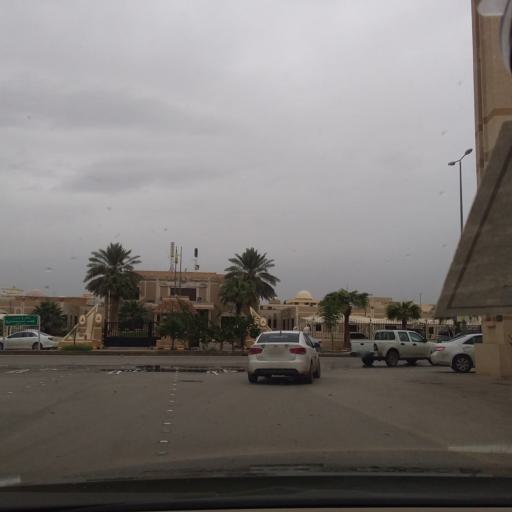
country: SA
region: Ar Riyad
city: Riyadh
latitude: 24.7292
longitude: 46.7745
